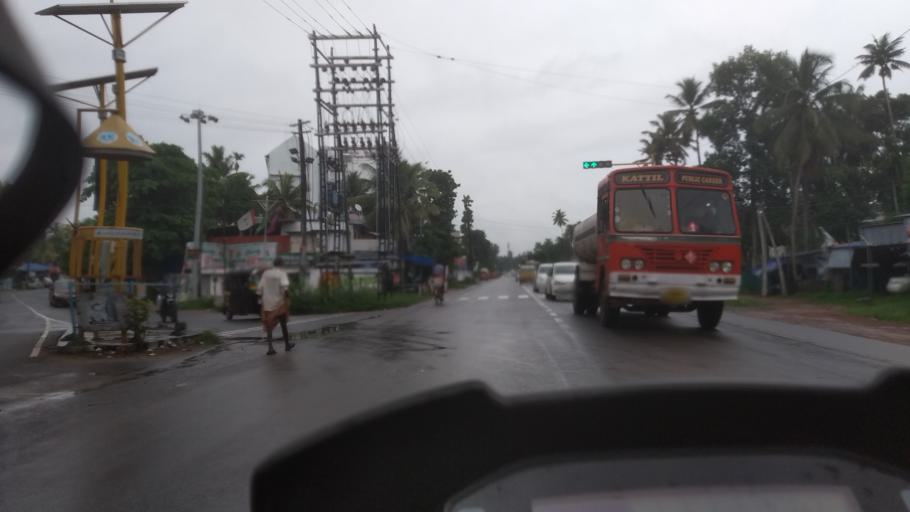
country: IN
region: Kerala
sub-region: Alappuzha
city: Kayankulam
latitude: 9.1298
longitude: 76.5152
